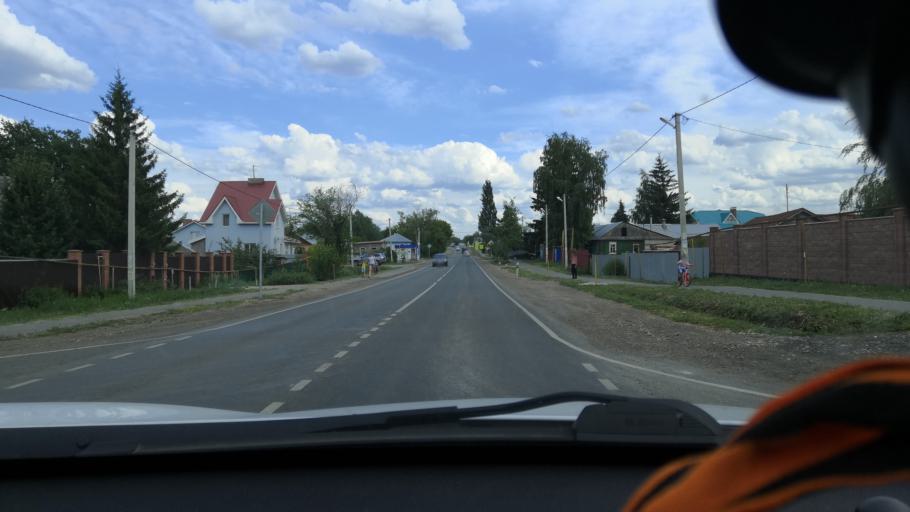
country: RU
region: Samara
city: Novosemeykino
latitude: 53.3792
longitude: 50.3430
